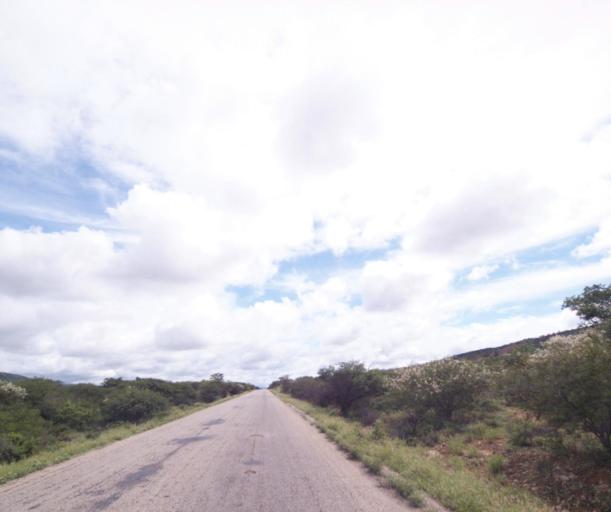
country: BR
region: Bahia
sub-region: Brumado
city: Brumado
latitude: -14.1893
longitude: -41.5764
